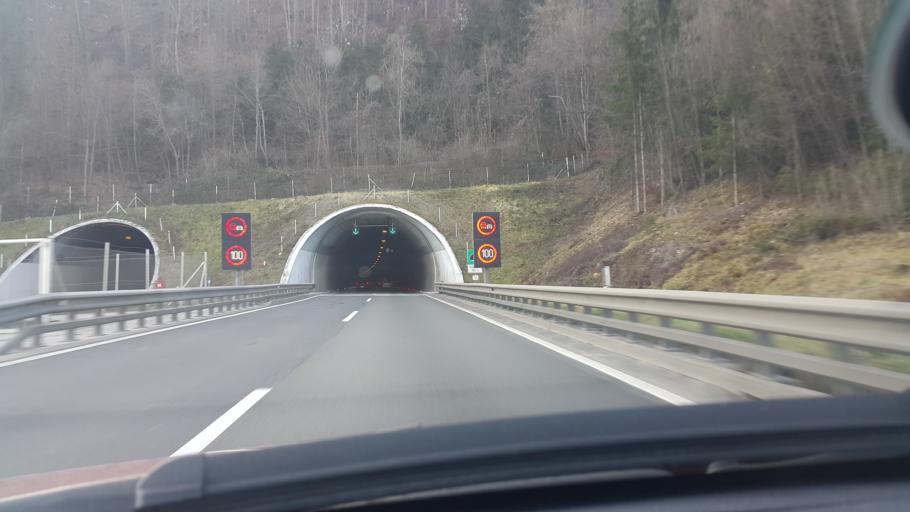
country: SI
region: Slovenska Konjice
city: Slovenske Konjice
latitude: 46.3175
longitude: 15.4594
